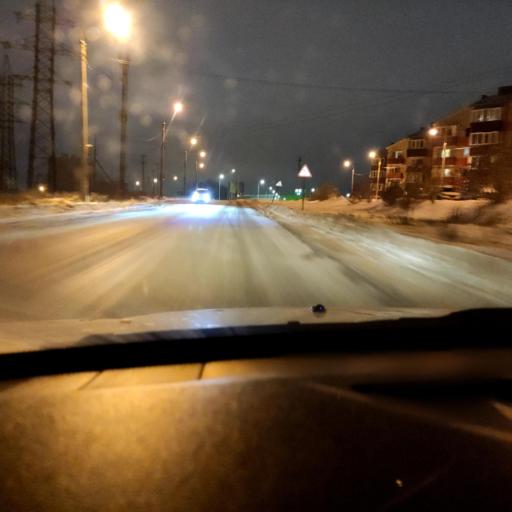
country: RU
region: Samara
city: Novosemeykino
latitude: 53.3295
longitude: 50.3131
